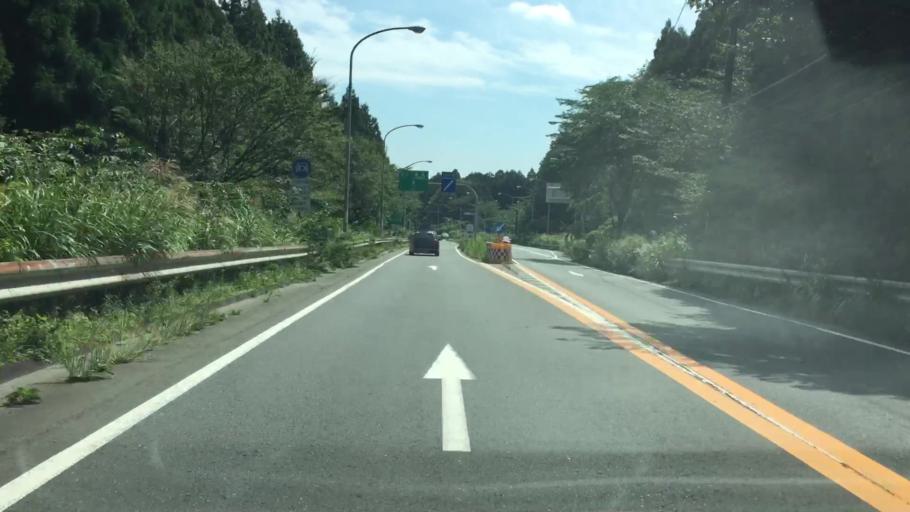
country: JP
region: Shizuoka
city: Fujinomiya
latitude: 35.3299
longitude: 138.5857
